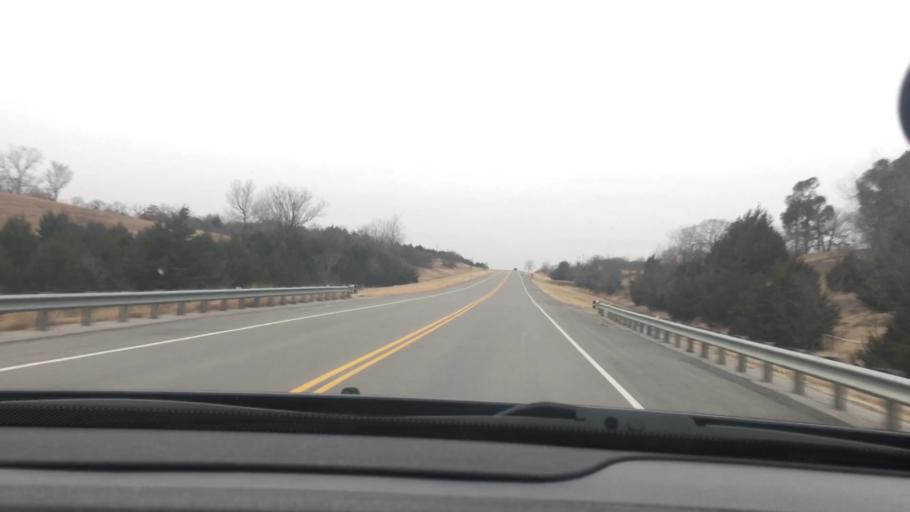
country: US
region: Oklahoma
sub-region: Garvin County
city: Wynnewood
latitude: 34.6227
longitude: -97.2026
